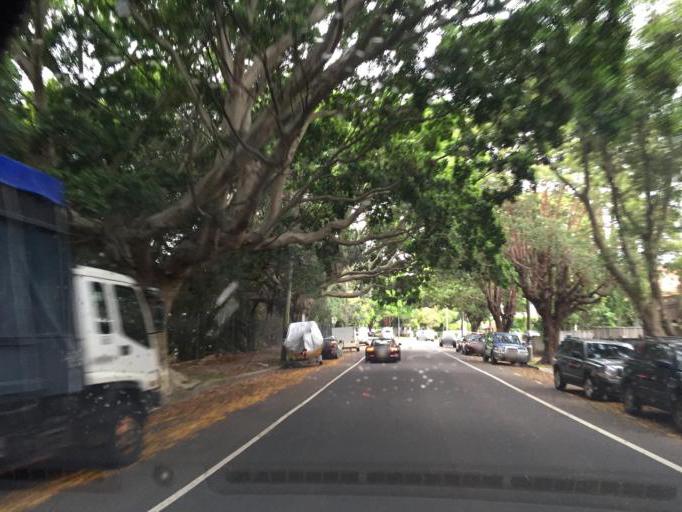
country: AU
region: New South Wales
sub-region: Waverley
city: North Bondi
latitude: -33.8817
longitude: 151.2640
